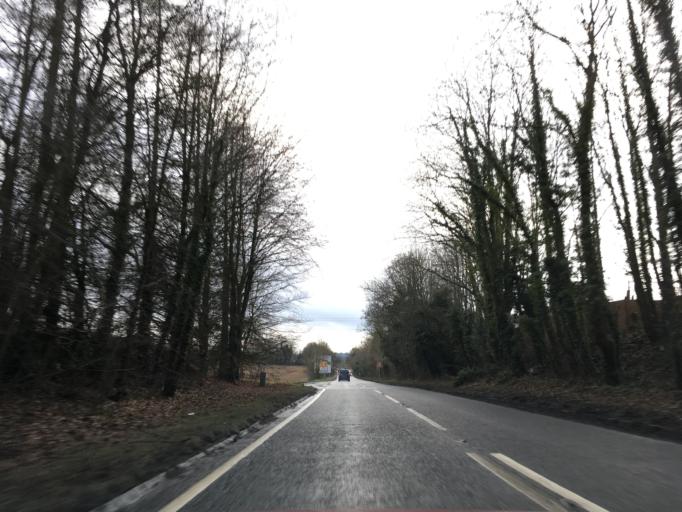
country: GB
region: England
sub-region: Gloucestershire
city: Charlton Kings
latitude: 51.8568
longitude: -2.0474
